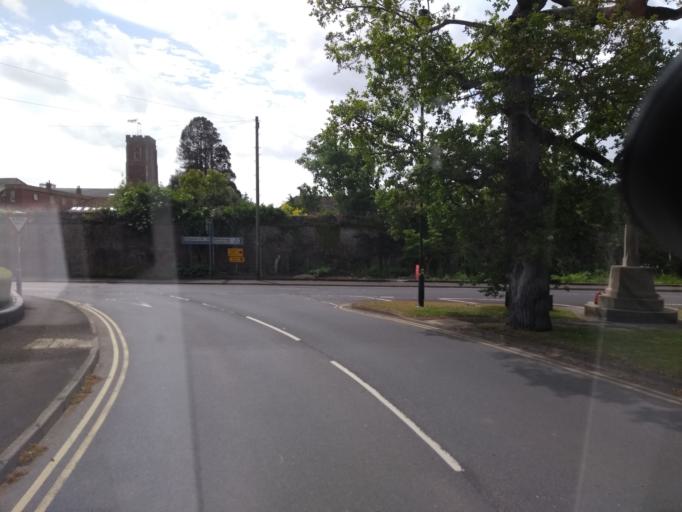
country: GB
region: England
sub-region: Somerset
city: Bridgwater
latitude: 51.1513
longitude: -3.0638
